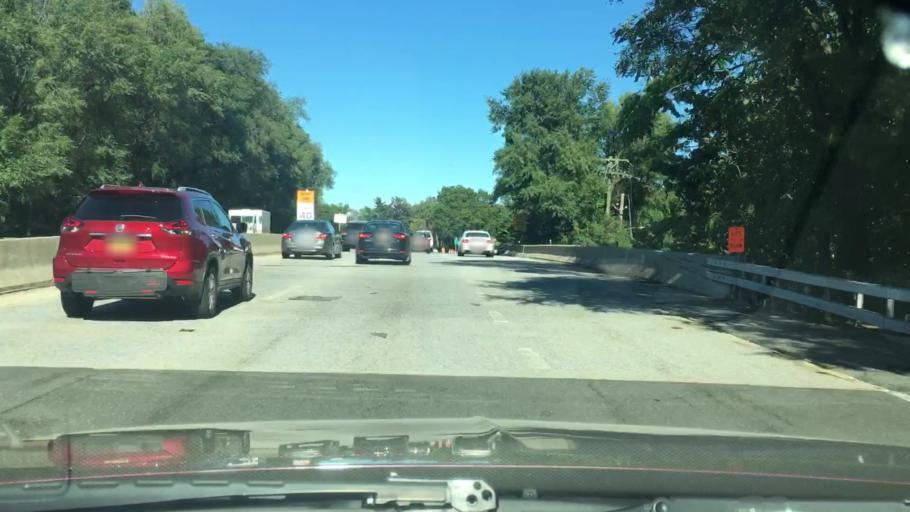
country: US
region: New York
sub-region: Westchester County
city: Pelham
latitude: 40.9024
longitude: -73.8150
